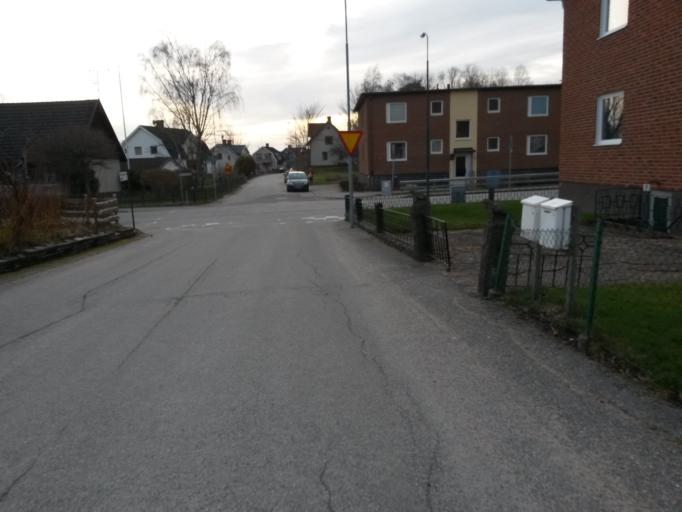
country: SE
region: Vaestra Goetaland
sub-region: Herrljunga Kommun
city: Herrljunga
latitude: 58.0756
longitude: 13.0287
